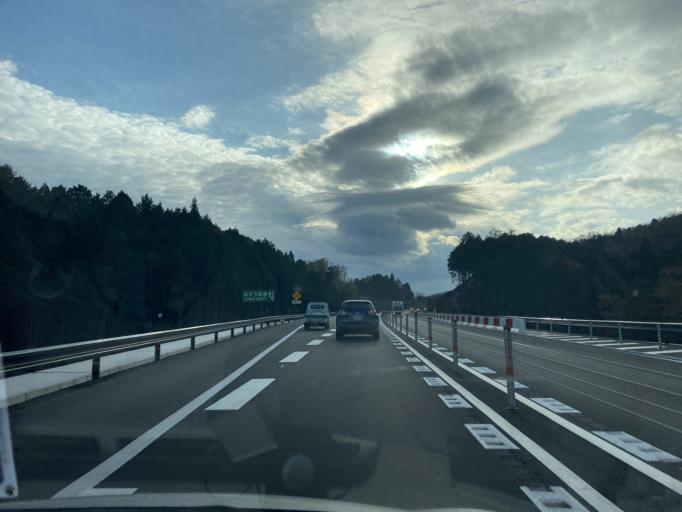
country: JP
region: Hyogo
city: Toyooka
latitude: 35.4914
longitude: 134.7815
